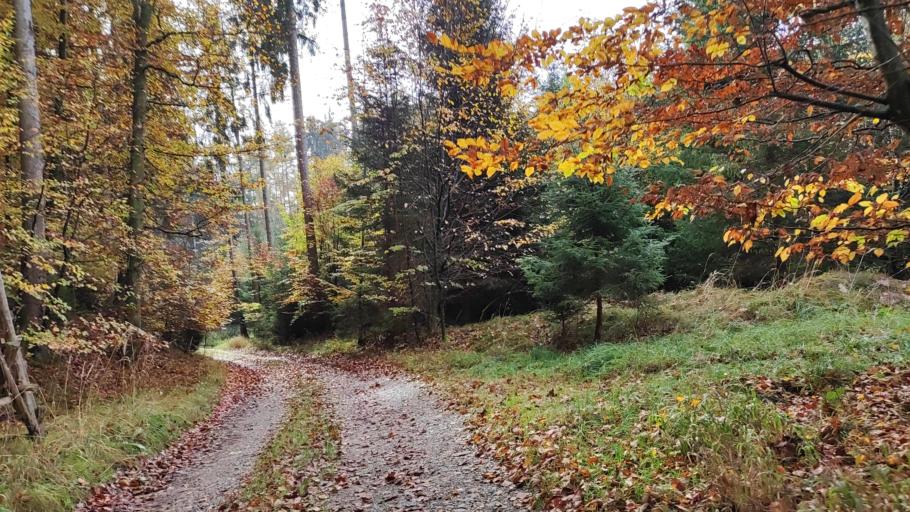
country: DE
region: Bavaria
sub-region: Swabia
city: Langenneufnach
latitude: 48.2899
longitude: 10.5982
